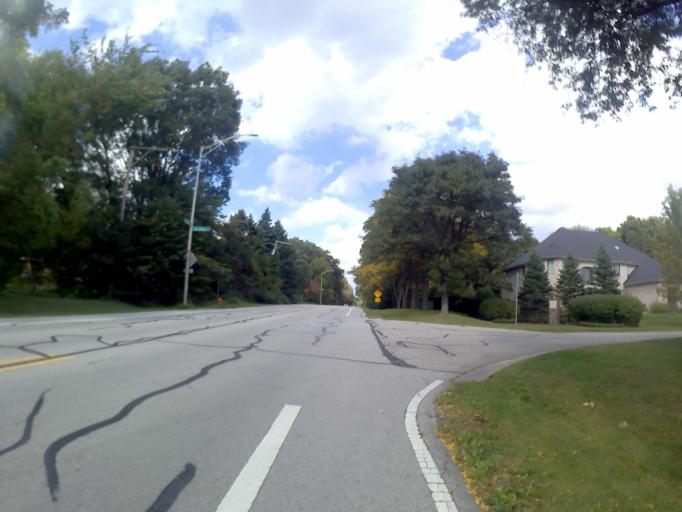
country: US
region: Illinois
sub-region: Will County
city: Bolingbrook
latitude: 41.7191
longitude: -88.1024
